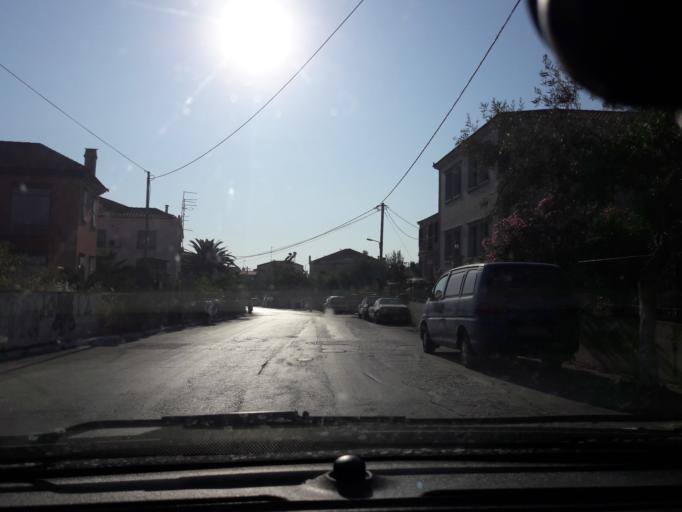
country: GR
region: North Aegean
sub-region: Nomos Lesvou
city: Myrina
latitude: 39.8723
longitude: 25.0647
